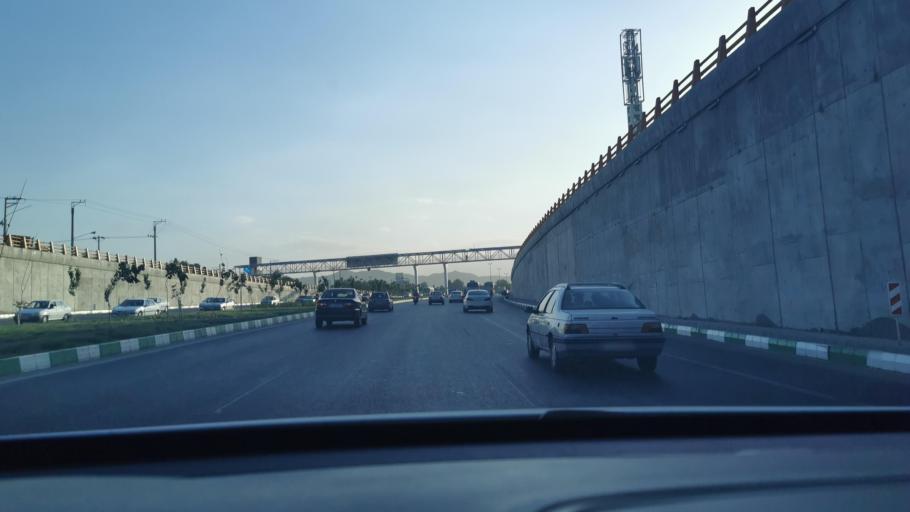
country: IR
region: Razavi Khorasan
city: Mashhad
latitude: 36.2595
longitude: 59.6446
